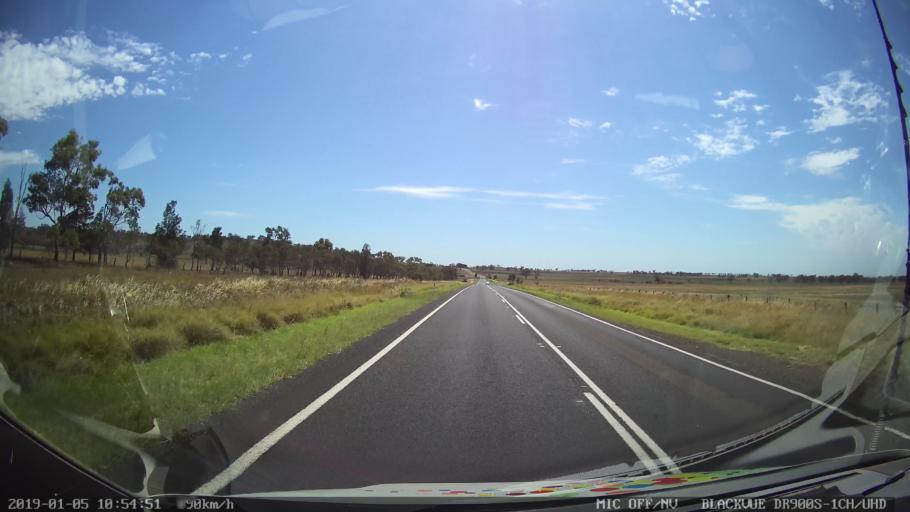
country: AU
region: New South Wales
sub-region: Warrumbungle Shire
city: Coonabarabran
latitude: -31.4508
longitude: 149.1341
